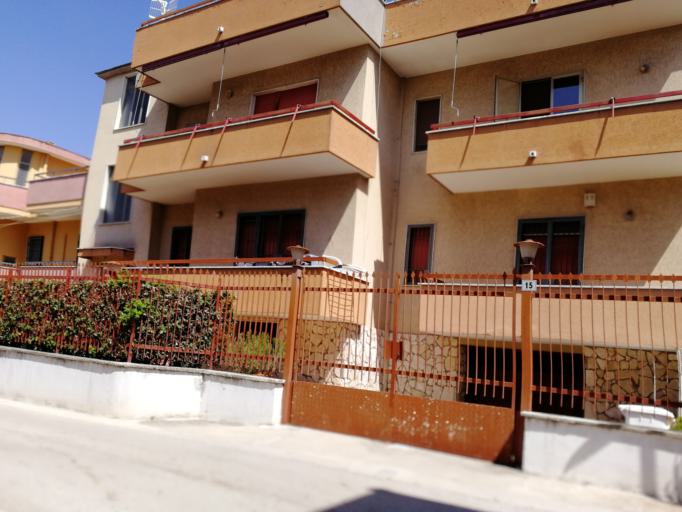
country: IT
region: Campania
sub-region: Provincia di Caserta
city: San Prisco
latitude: 41.0886
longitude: 14.2784
